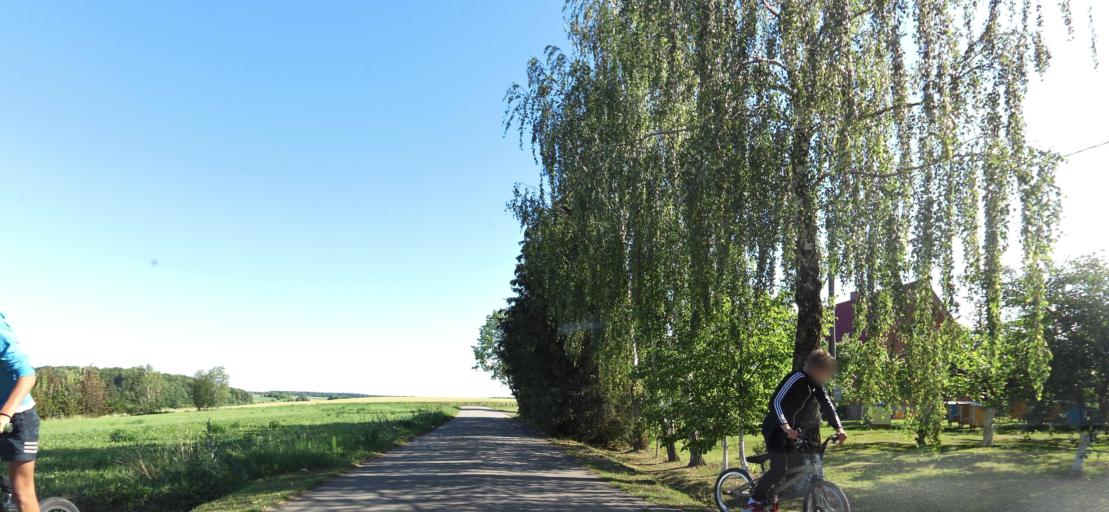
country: LT
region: Panevezys
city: Pasvalys
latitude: 56.1534
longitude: 24.4476
